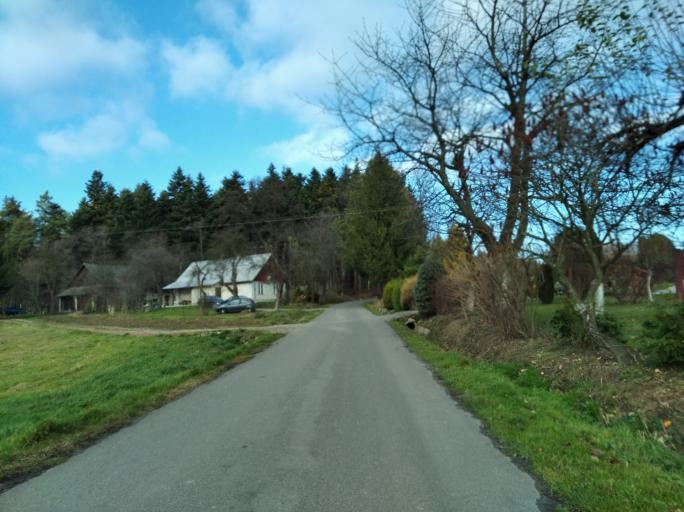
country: PL
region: Subcarpathian Voivodeship
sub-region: Powiat strzyzowski
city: Babica
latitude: 49.9073
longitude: 21.8498
